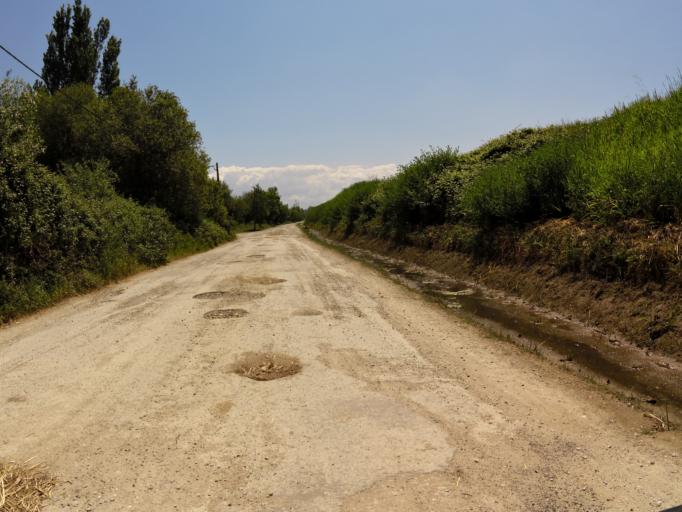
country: PT
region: Coimbra
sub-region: Montemor-O-Velho
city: Montemor-o-Velho
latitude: 40.1484
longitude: -8.7161
